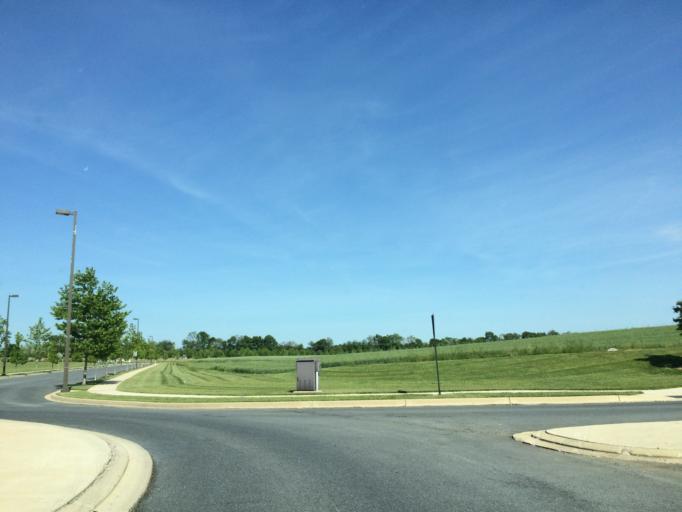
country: US
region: Maryland
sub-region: Frederick County
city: Spring Ridge
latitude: 39.4379
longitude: -77.3668
